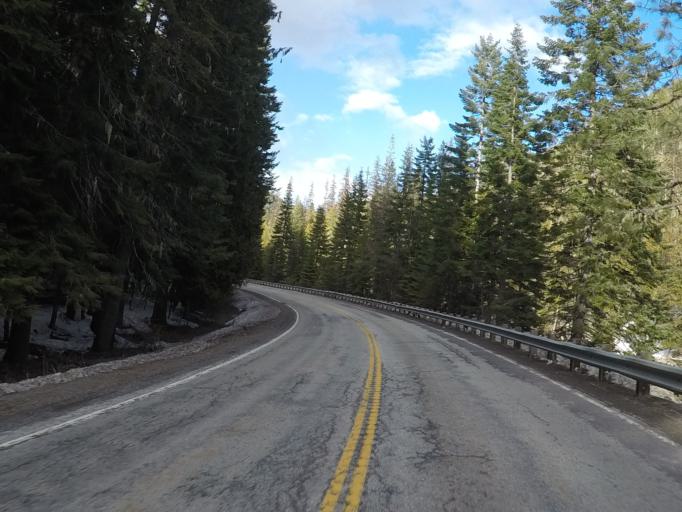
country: US
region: Montana
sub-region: Mineral County
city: Superior
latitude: 46.4889
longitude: -114.8709
